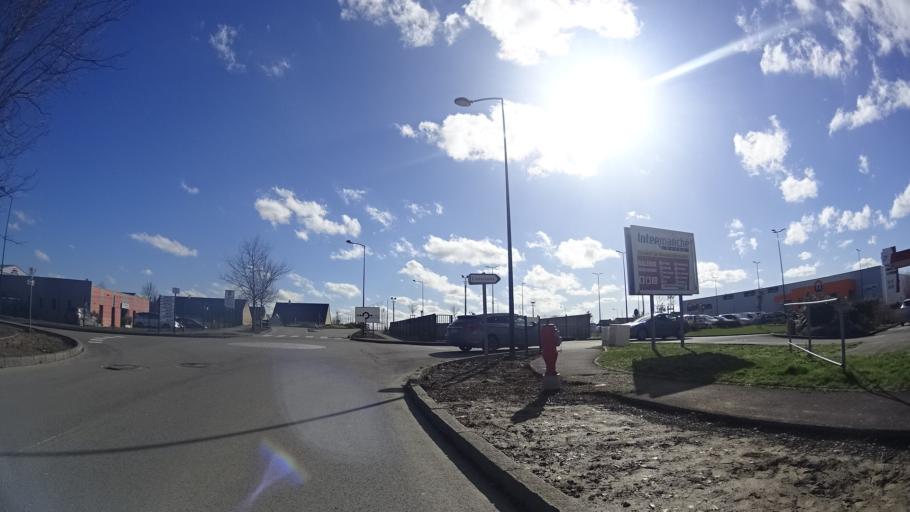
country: FR
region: Brittany
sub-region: Departement d'Ille-et-Vilaine
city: Combourg
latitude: 48.4174
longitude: -1.7489
